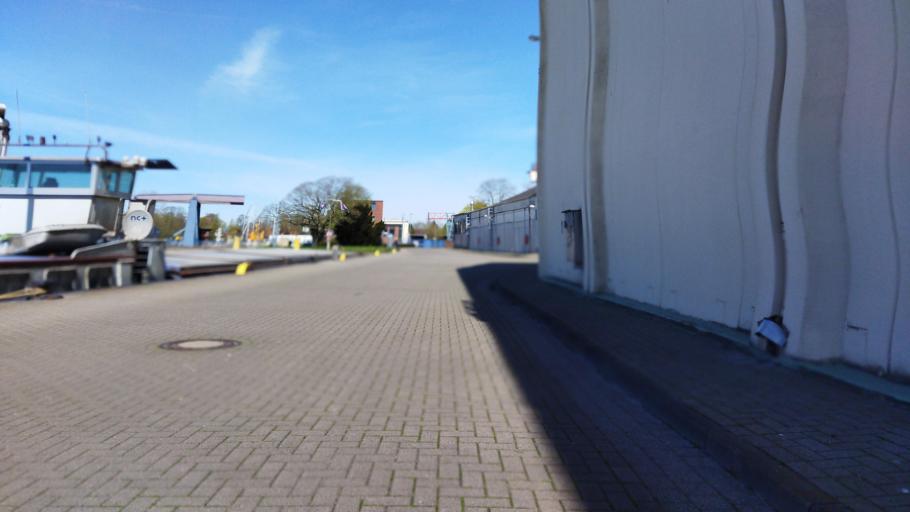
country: DE
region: Lower Saxony
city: Brake (Unterweser)
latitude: 53.3306
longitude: 8.4856
